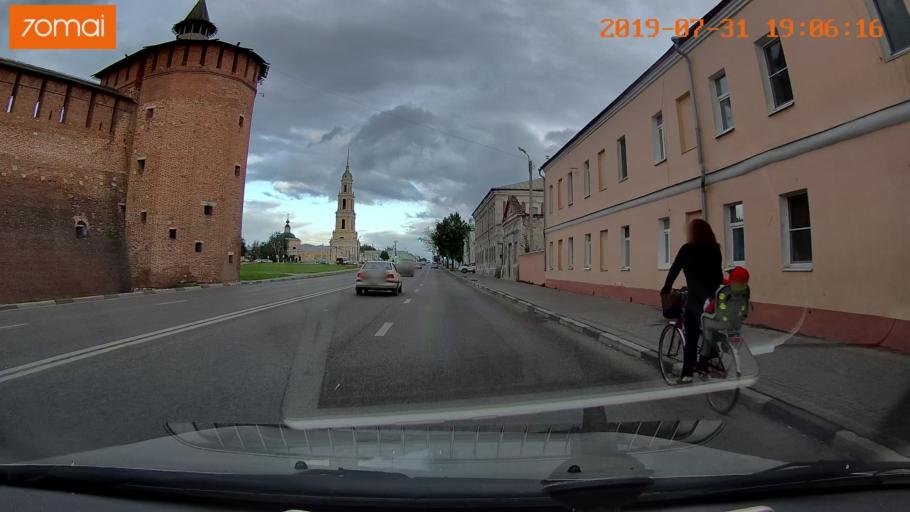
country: RU
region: Moskovskaya
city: Kolomna
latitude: 55.1032
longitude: 38.7515
